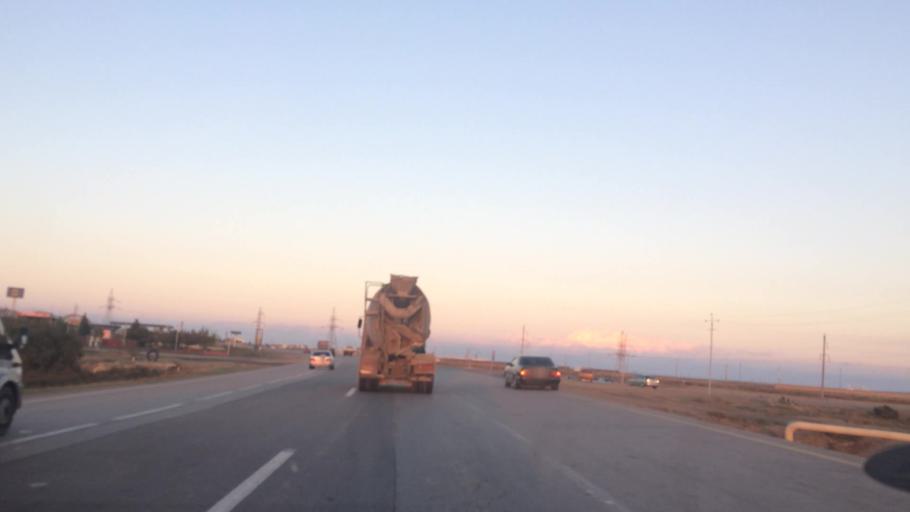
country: AZ
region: Baki
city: Qobustan
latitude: 39.9644
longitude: 49.4056
